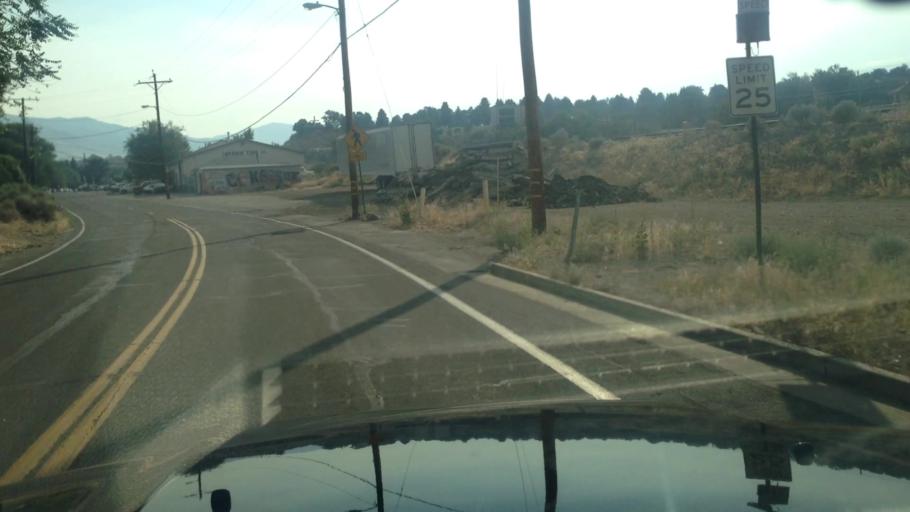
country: US
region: Nevada
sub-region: Washoe County
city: Reno
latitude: 39.5236
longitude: -119.8347
